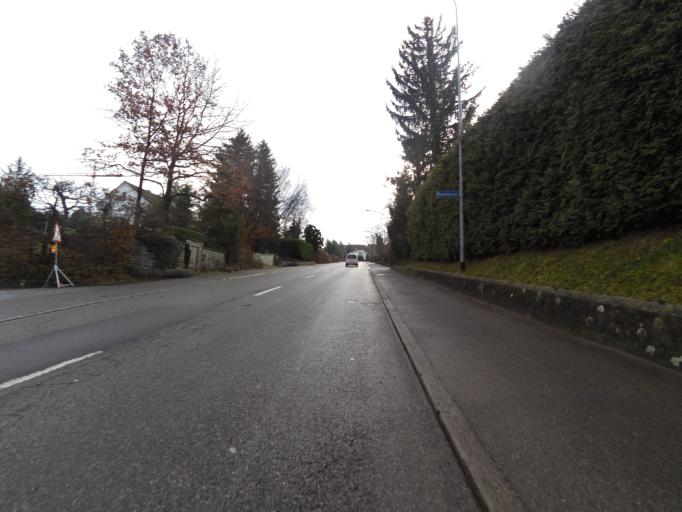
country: CH
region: Thurgau
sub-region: Frauenfeld District
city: Frauenfeld
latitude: 47.5503
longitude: 8.9048
